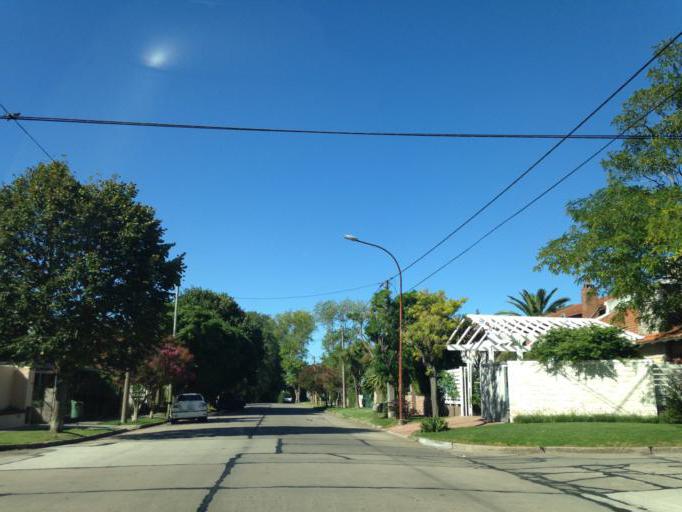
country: AR
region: Buenos Aires
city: Mar del Plata
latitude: -38.0278
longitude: -57.5444
